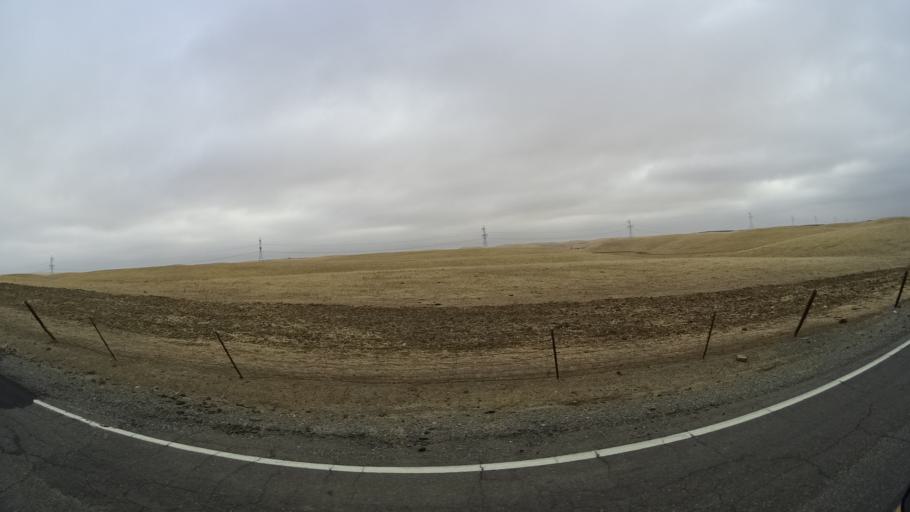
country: US
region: California
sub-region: Yolo County
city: Dunnigan
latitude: 38.8342
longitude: -122.0436
